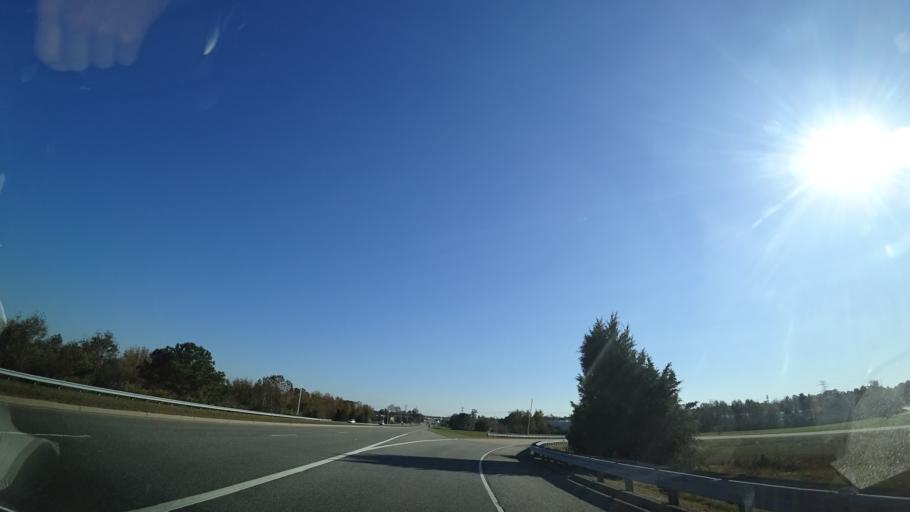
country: US
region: Virginia
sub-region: City of Portsmouth
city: Portsmouth Heights
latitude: 36.8857
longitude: -76.4285
